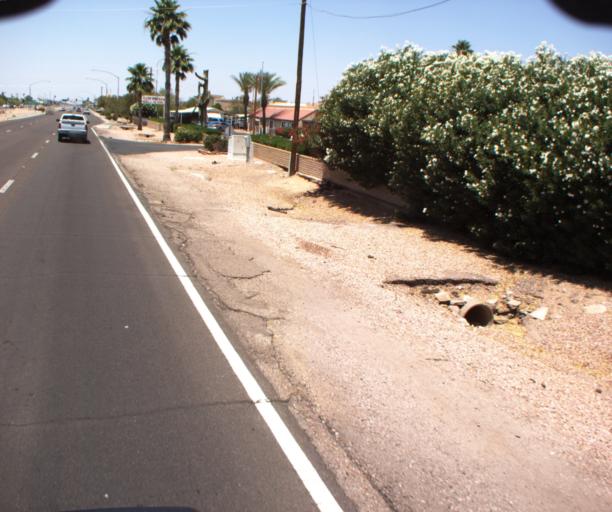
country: US
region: Arizona
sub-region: Pinal County
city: Apache Junction
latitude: 33.4154
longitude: -111.6291
